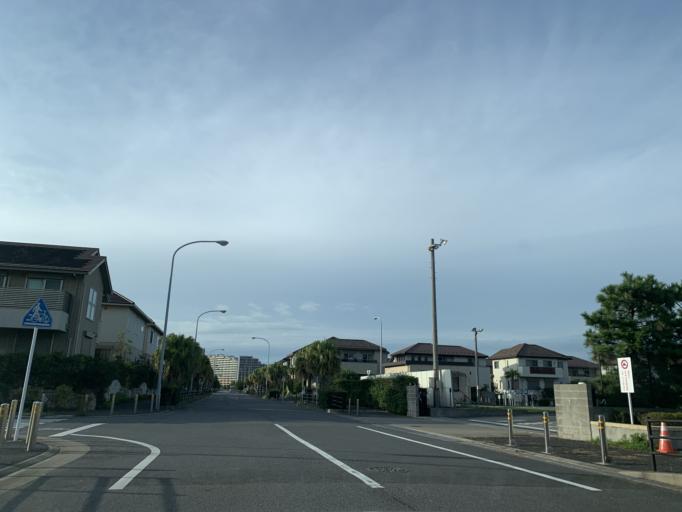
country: JP
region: Tokyo
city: Urayasu
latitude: 35.6420
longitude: 139.9353
